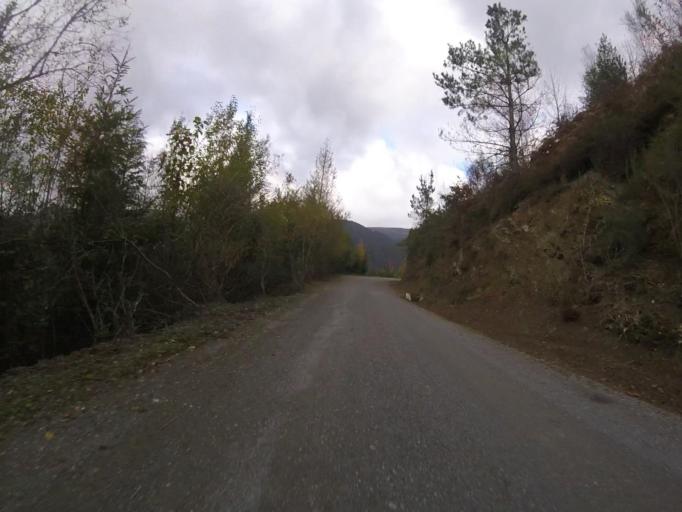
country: ES
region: Navarre
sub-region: Provincia de Navarra
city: Goizueta
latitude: 43.2215
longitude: -1.8332
